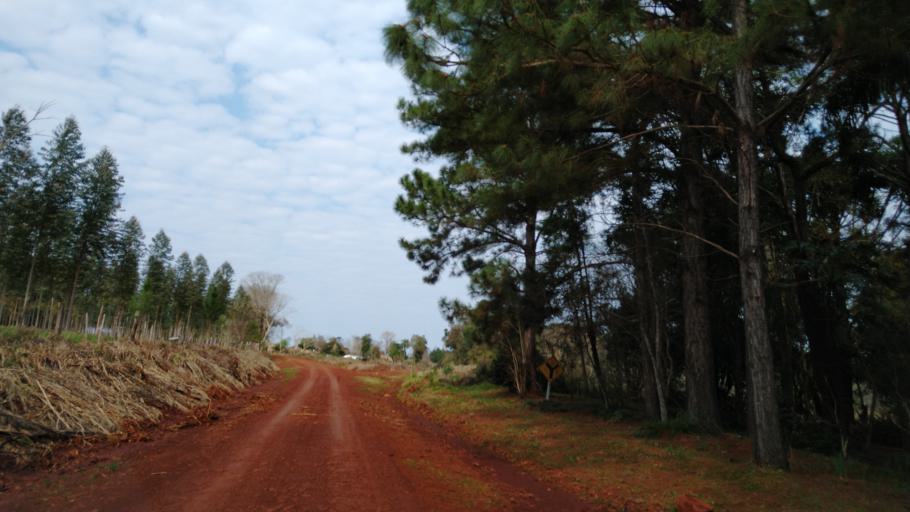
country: AR
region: Misiones
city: Capiovi
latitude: -26.9477
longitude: -55.0675
